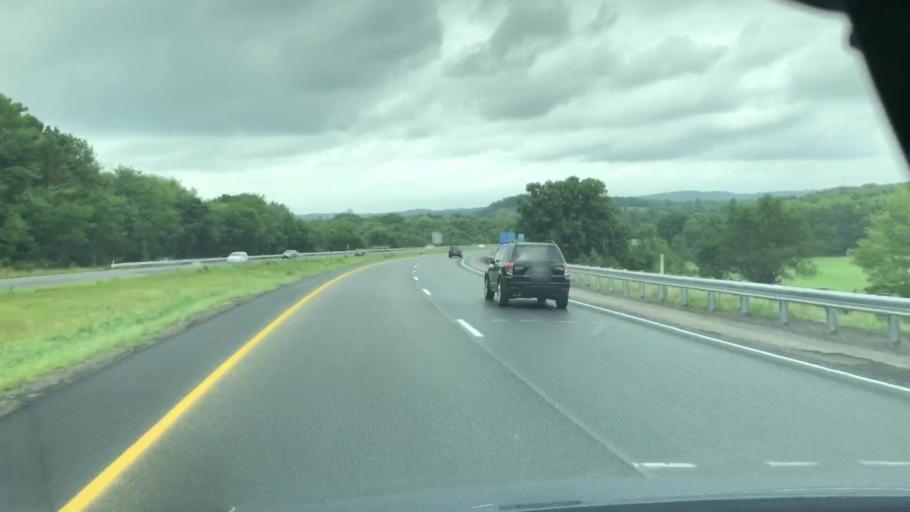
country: US
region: Pennsylvania
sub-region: Butler County
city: Prospect
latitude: 40.9474
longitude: -80.1435
